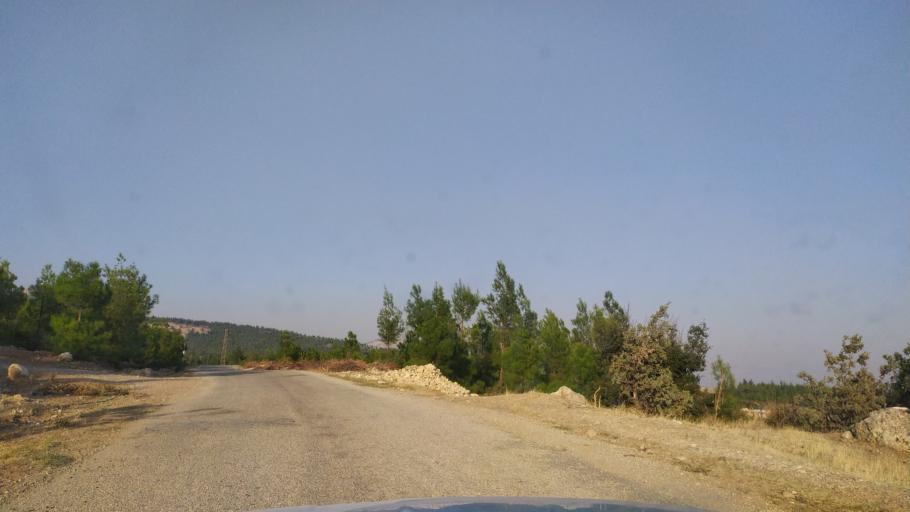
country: TR
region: Mersin
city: Mut
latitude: 36.6847
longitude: 33.1938
